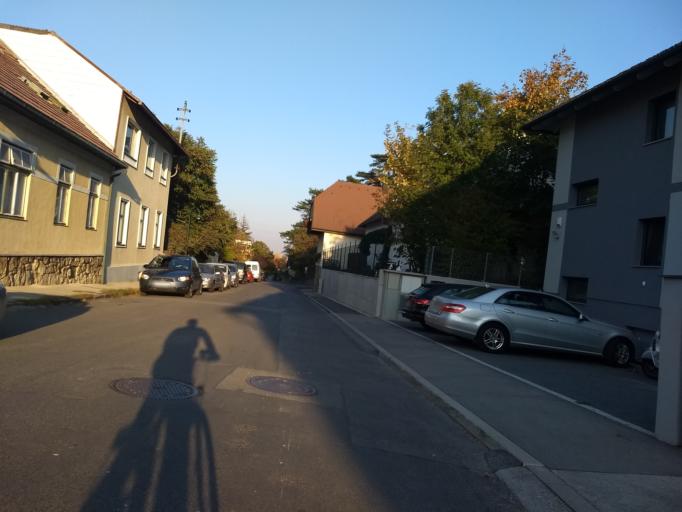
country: AT
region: Lower Austria
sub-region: Politischer Bezirk Modling
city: Perchtoldsdorf
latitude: 48.1217
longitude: 16.2582
